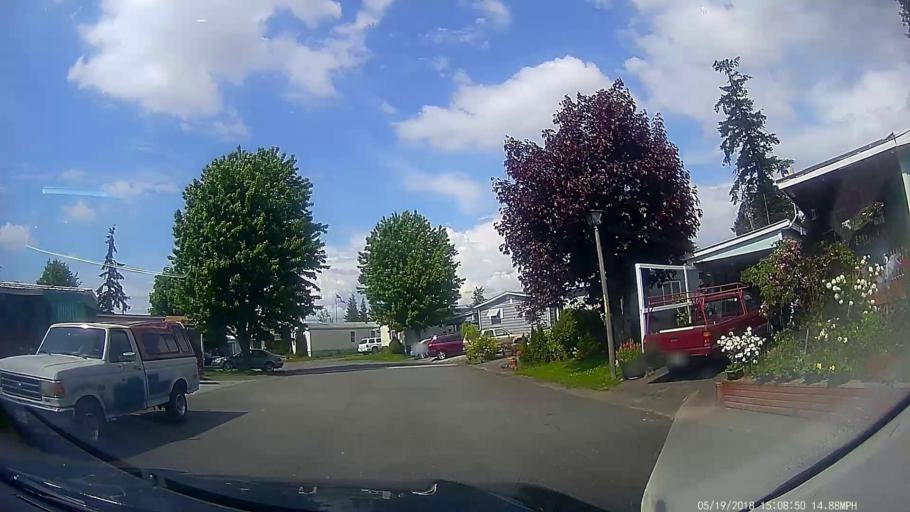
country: US
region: Washington
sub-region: Skagit County
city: Mount Vernon
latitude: 48.4201
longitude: -122.3070
